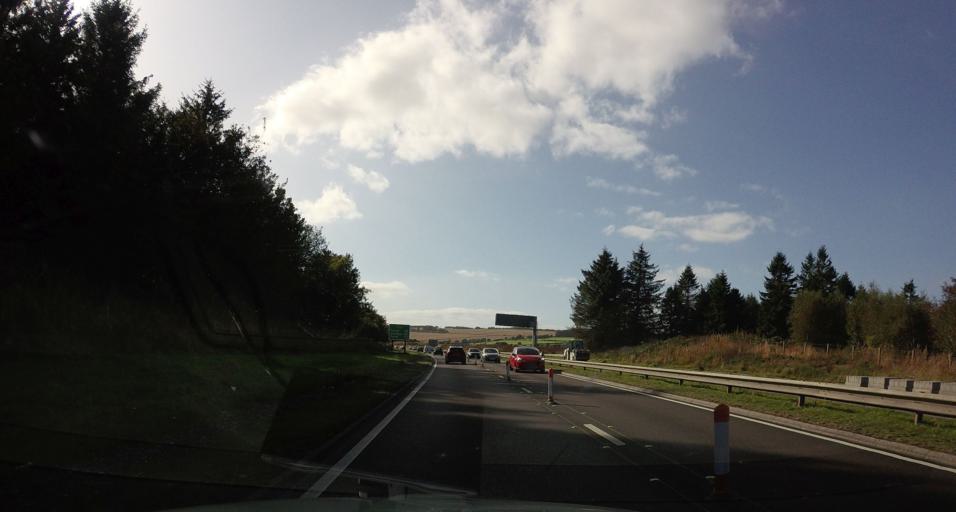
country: GB
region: Scotland
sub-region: Aberdeenshire
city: Stonehaven
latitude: 56.9758
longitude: -2.2239
